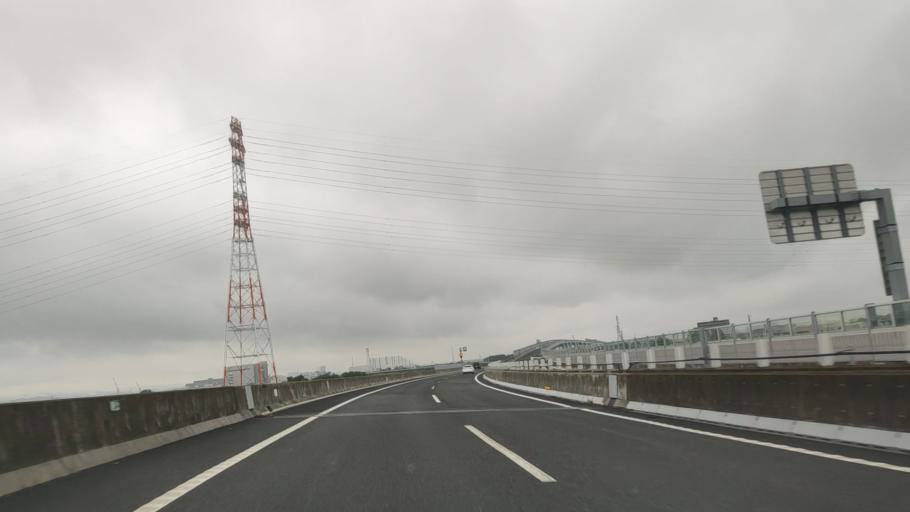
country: JP
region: Kanagawa
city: Chigasaki
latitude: 35.3664
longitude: 139.3730
